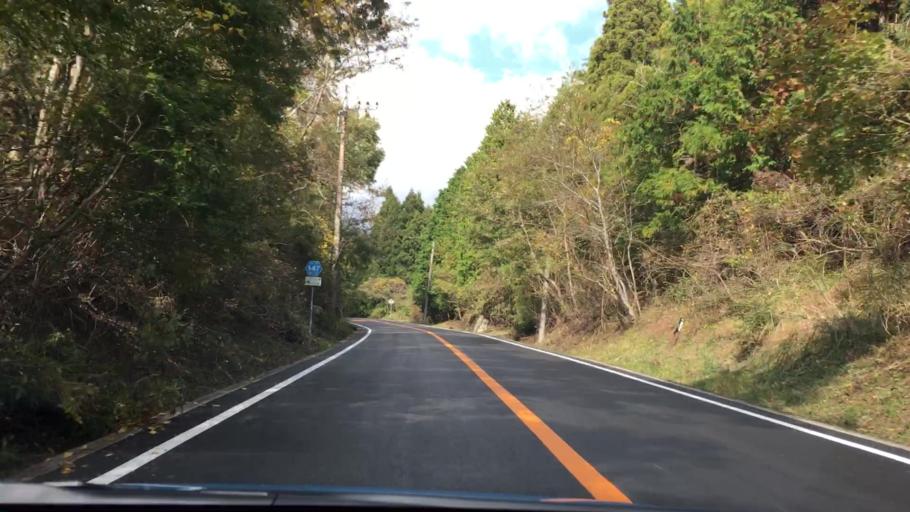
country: JP
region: Shizuoka
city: Gotemba
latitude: 35.3798
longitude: 138.9439
